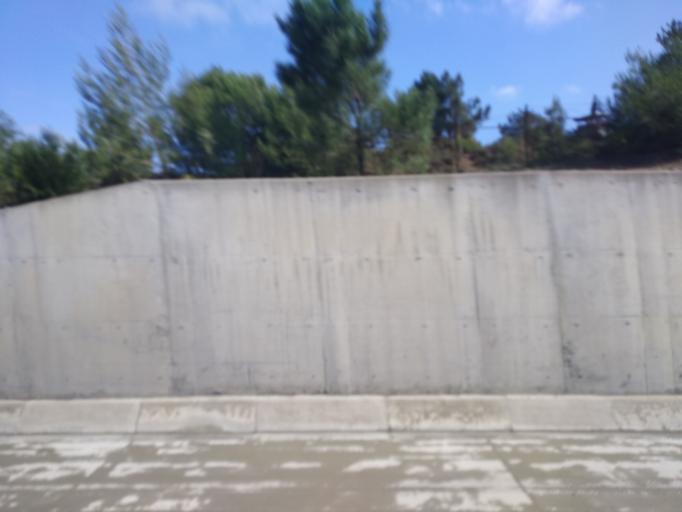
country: TR
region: Istanbul
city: Kemerburgaz
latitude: 41.1268
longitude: 28.9452
